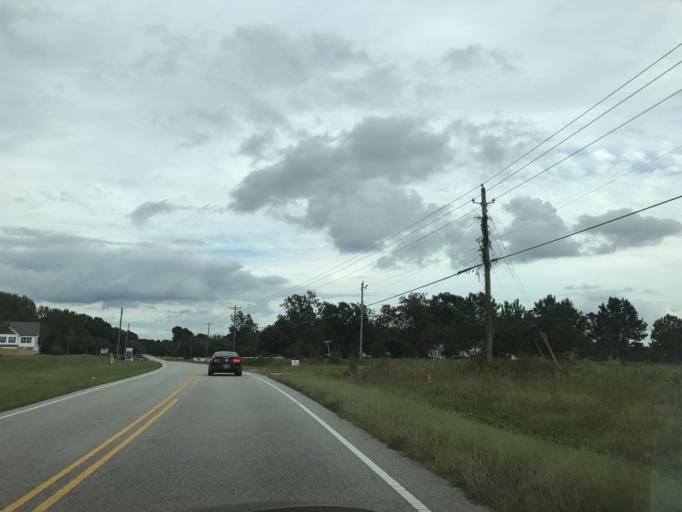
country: US
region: North Carolina
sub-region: Franklin County
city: Youngsville
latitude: 35.9898
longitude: -78.4036
